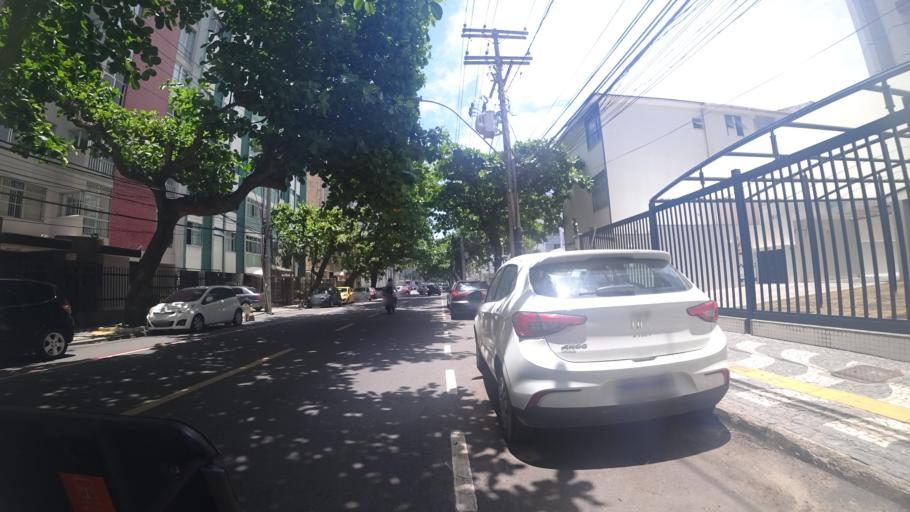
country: BR
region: Bahia
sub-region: Salvador
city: Salvador
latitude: -13.0081
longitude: -38.4654
